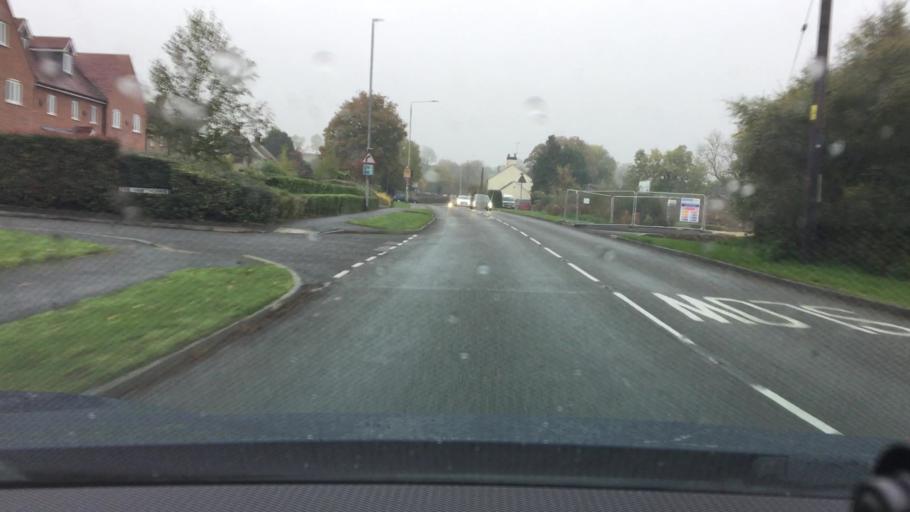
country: GB
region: England
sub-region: Leicestershire
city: Market Harborough
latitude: 52.4783
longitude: -0.9677
